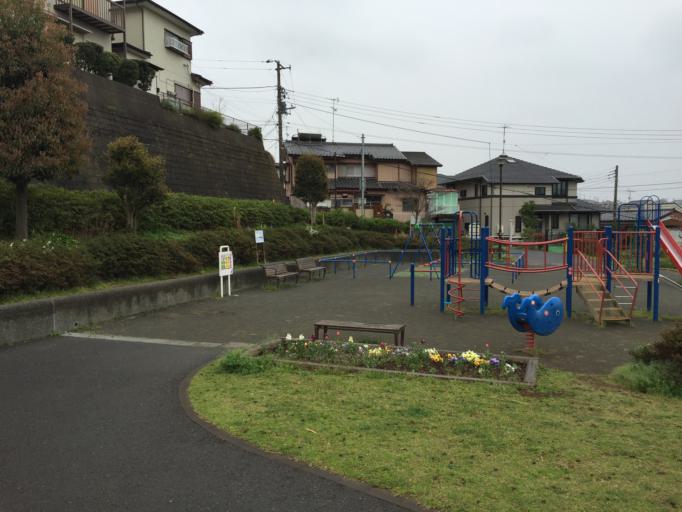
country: JP
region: Kanagawa
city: Yokohama
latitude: 35.4213
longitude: 139.5891
